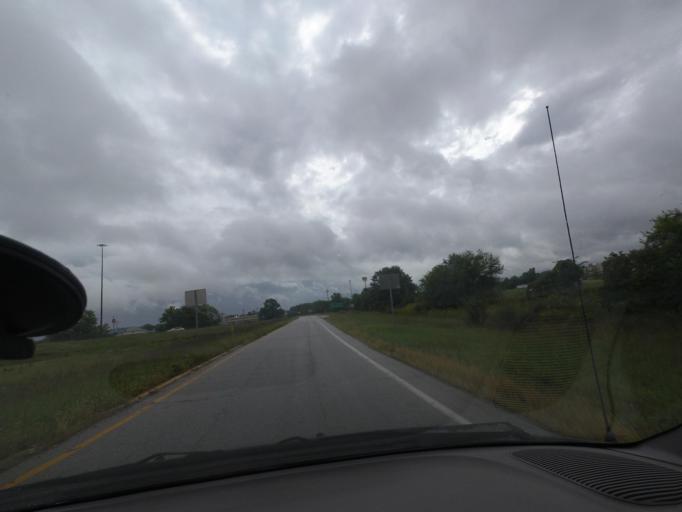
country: US
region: Indiana
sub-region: Montgomery County
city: Crawfordsville
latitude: 40.0796
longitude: -86.9071
